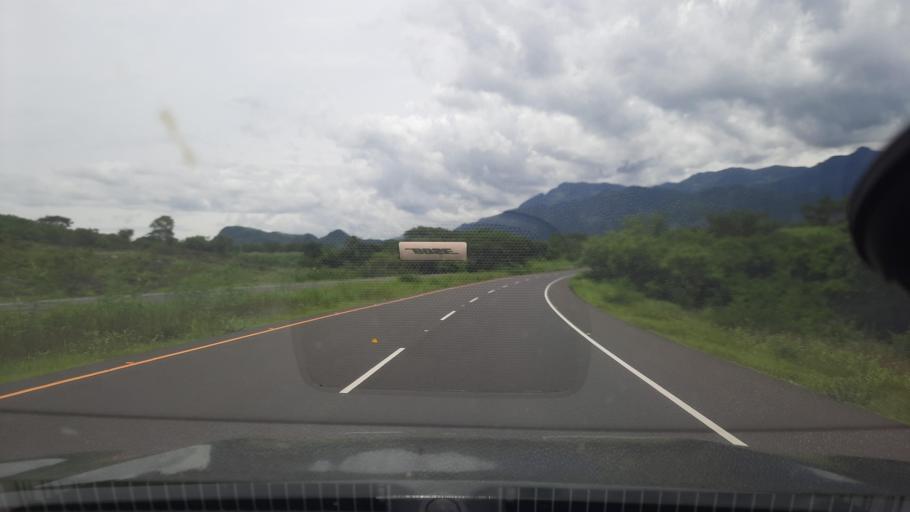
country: HN
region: Valle
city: Aramecina
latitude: 13.7666
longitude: -87.7063
